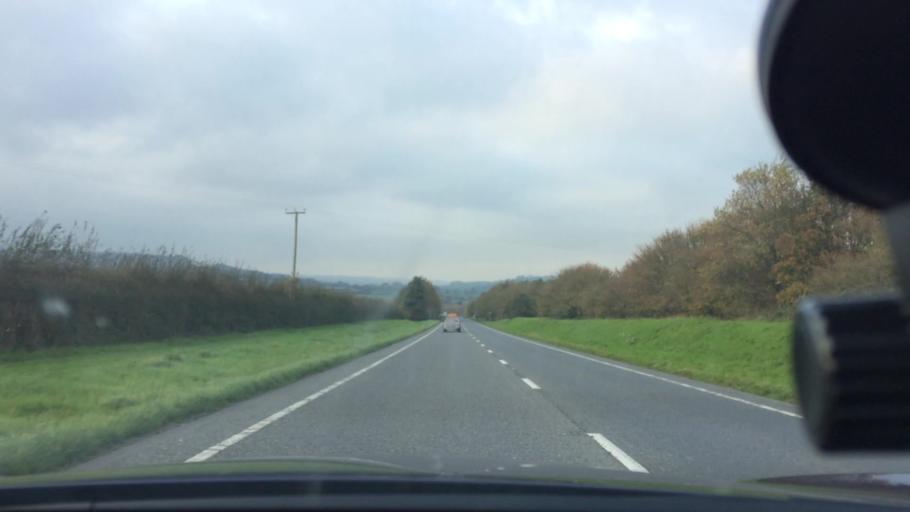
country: GB
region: England
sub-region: Devon
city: Axminster
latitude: 50.7716
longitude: -3.0077
